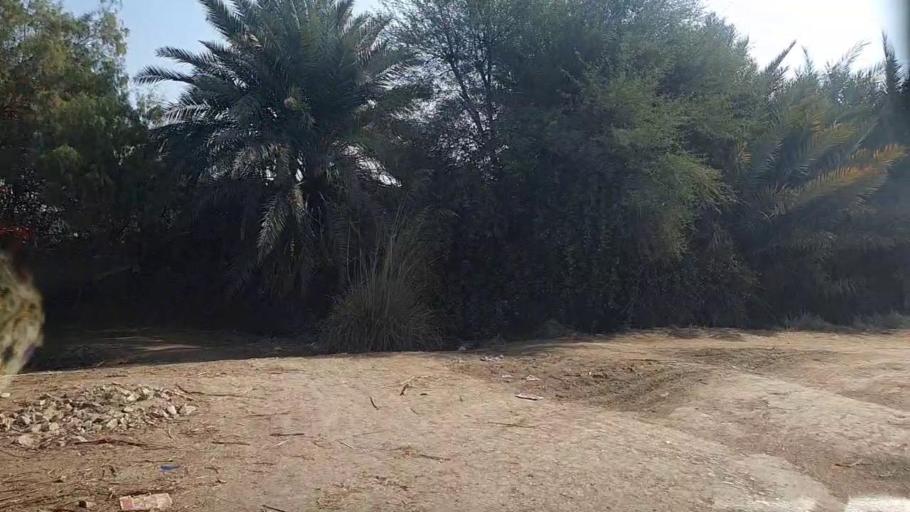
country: PK
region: Sindh
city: Khairpur
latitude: 27.9384
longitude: 69.6714
